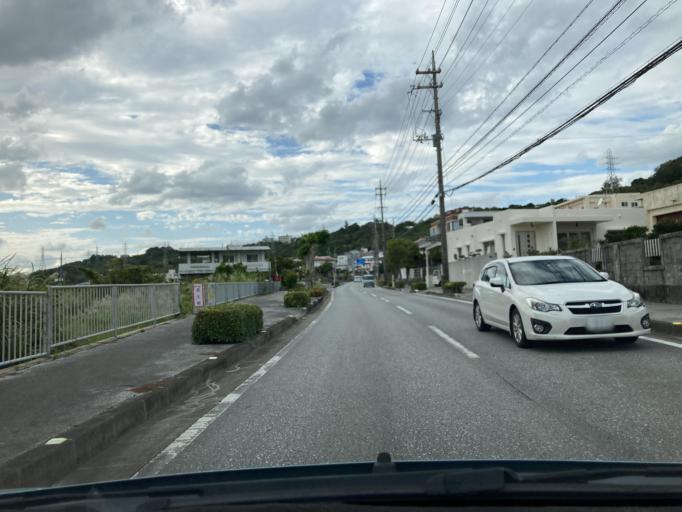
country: JP
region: Okinawa
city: Gushikawa
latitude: 26.3477
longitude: 127.8650
